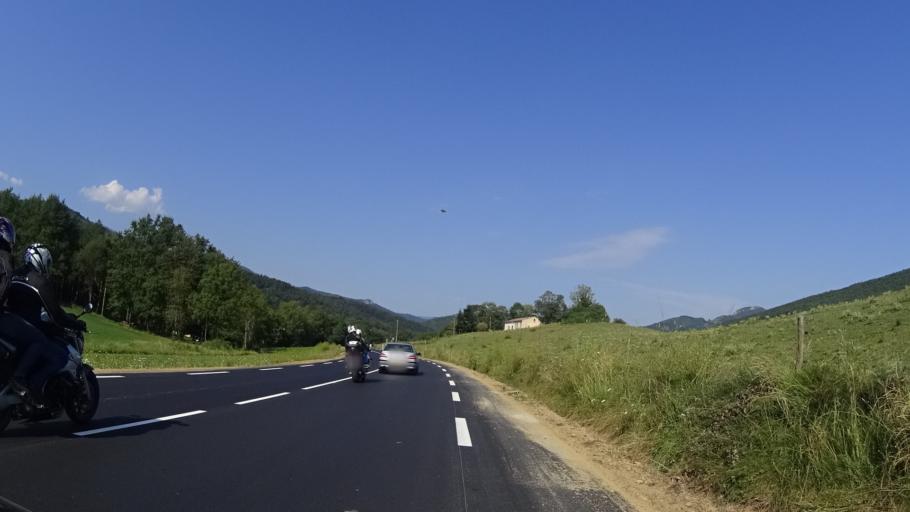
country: FR
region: Midi-Pyrenees
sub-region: Departement de l'Ariege
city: Lavelanet
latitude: 42.9159
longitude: 1.8188
